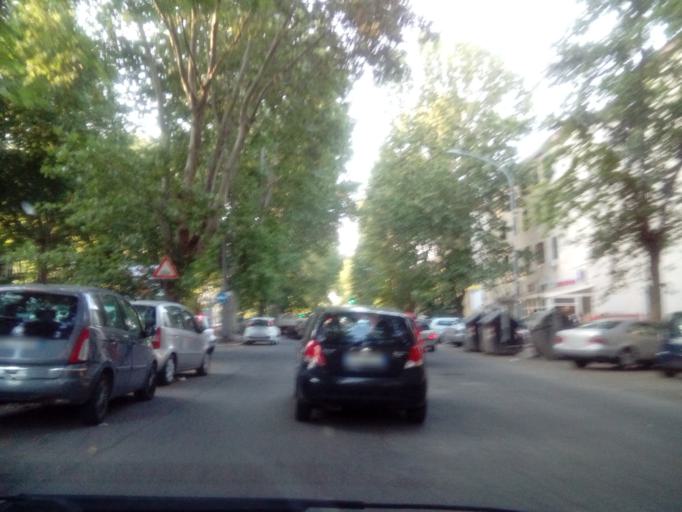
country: IT
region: Latium
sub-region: Citta metropolitana di Roma Capitale
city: Rome
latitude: 41.8920
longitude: 12.5746
